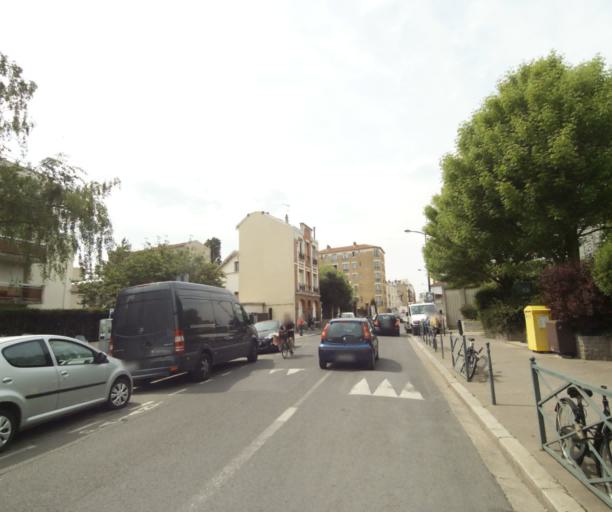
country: FR
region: Ile-de-France
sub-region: Departement des Hauts-de-Seine
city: Asnieres-sur-Seine
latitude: 48.9141
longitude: 2.2802
